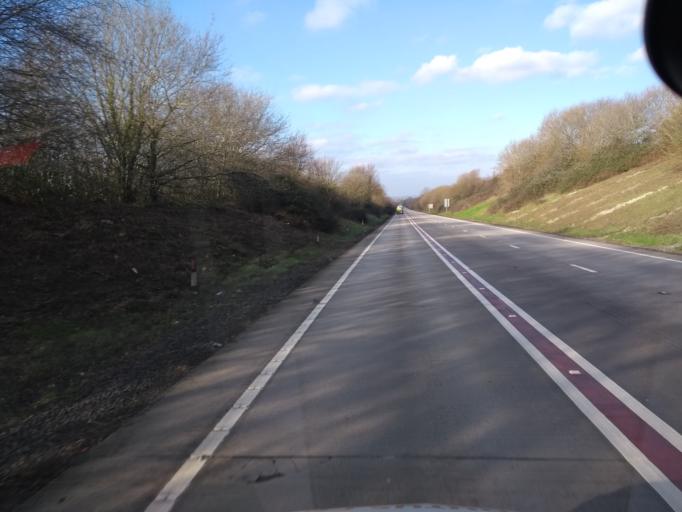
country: GB
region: England
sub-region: Somerset
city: Ilminster
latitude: 50.9348
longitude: -2.8697
